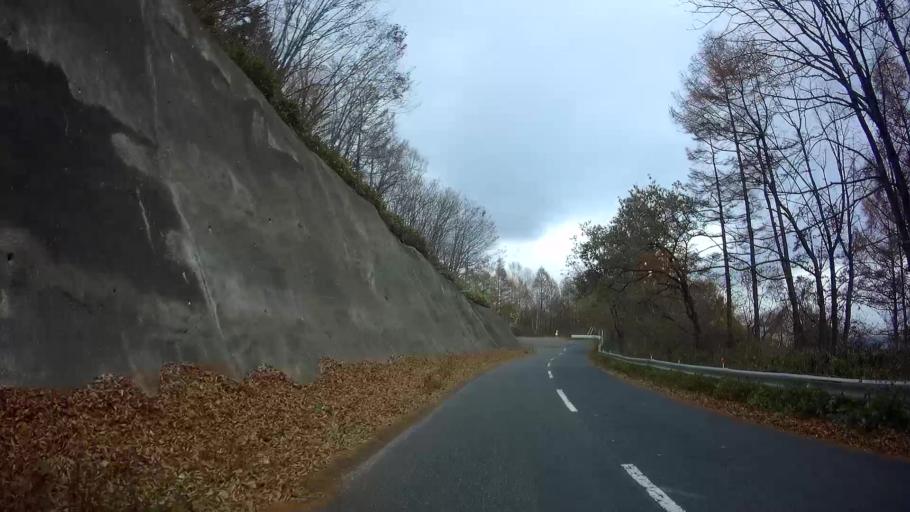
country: JP
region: Gunma
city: Nakanojomachi
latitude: 36.6813
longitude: 138.6627
